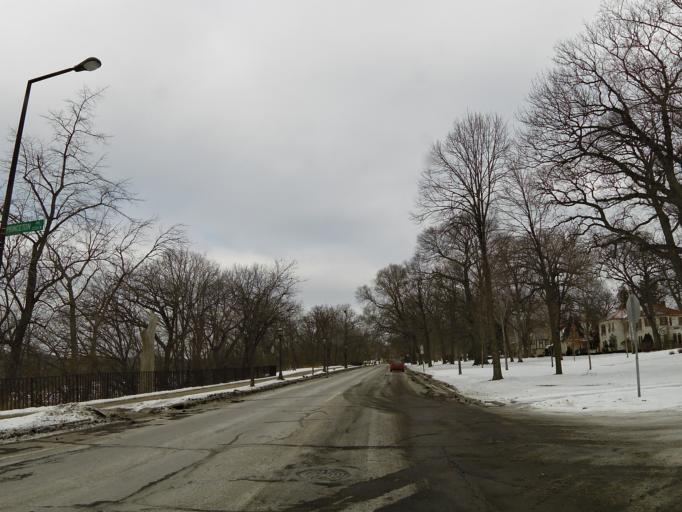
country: US
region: Minnesota
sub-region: Ramsey County
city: Lauderdale
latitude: 44.9360
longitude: -93.1983
